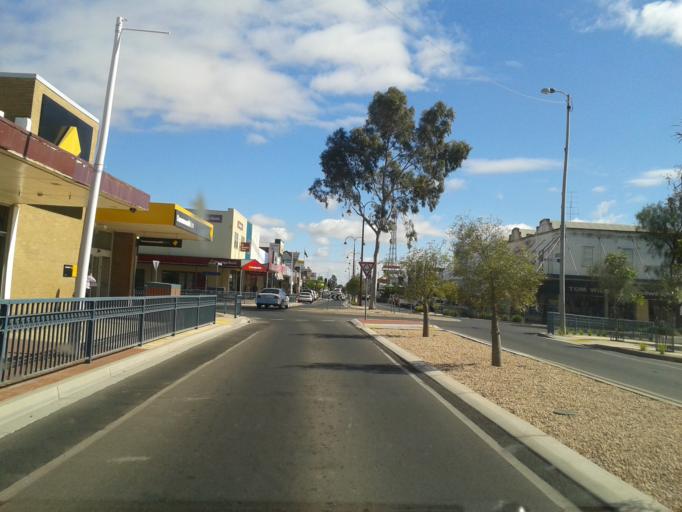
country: AU
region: Victoria
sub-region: Swan Hill
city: Swan Hill
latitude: -35.3412
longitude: 143.5601
